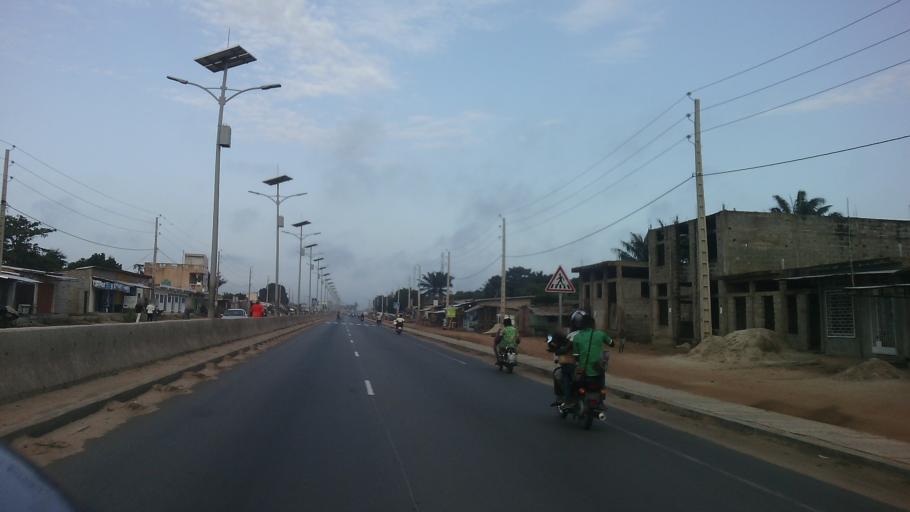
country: BJ
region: Atlantique
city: Hevie
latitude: 6.3857
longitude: 2.2165
